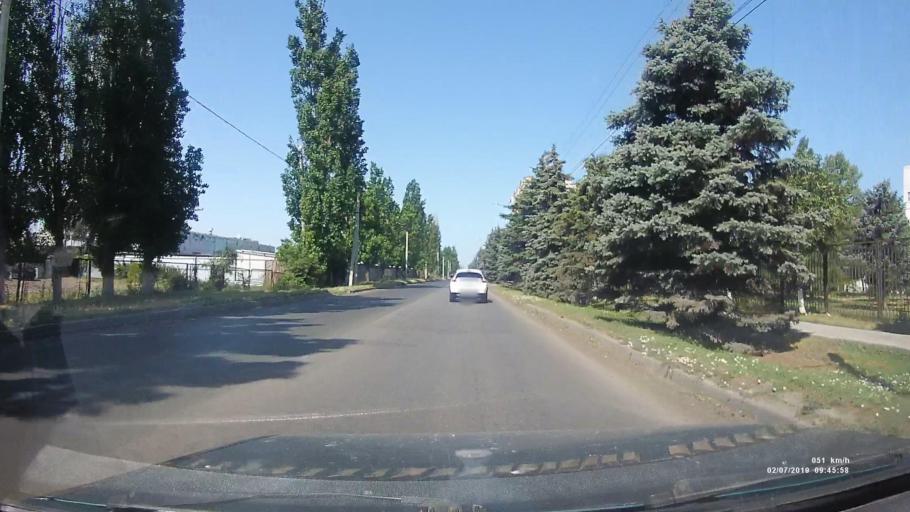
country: RU
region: Rostov
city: Azov
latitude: 47.1020
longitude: 39.4086
